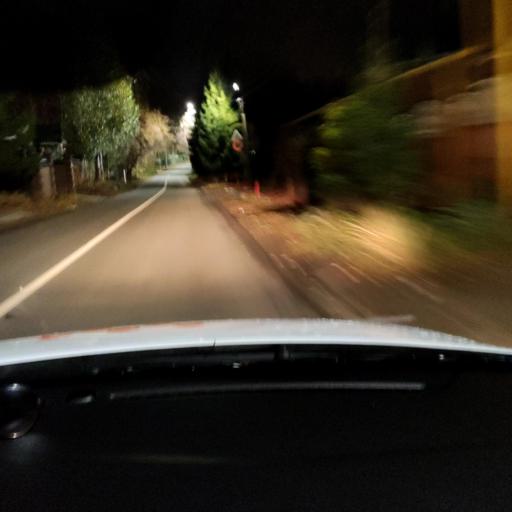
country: RU
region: Tatarstan
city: Verkhniy Uslon
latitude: 55.6231
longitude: 49.0138
